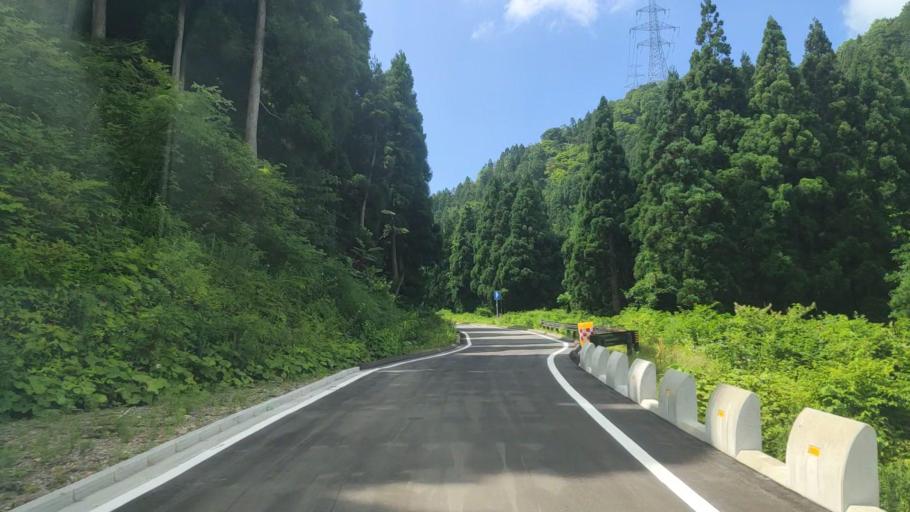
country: JP
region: Fukui
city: Katsuyama
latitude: 36.1578
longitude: 136.5265
